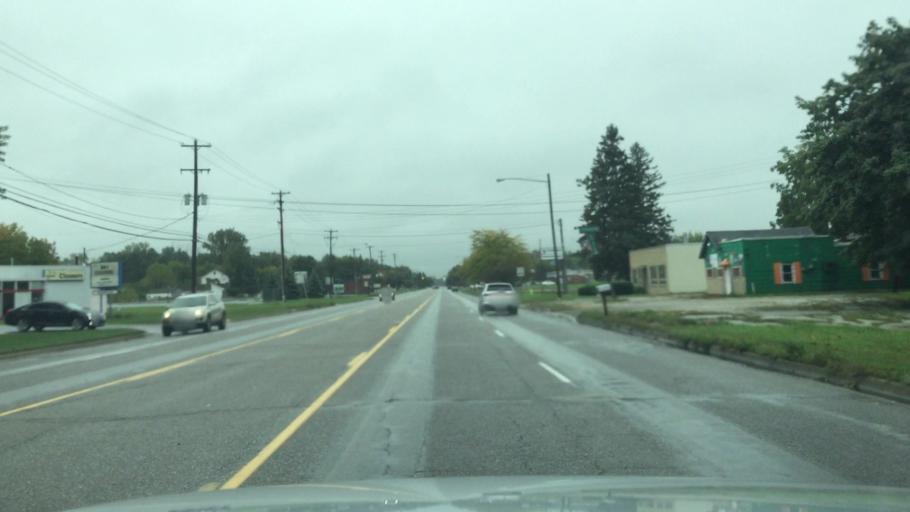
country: US
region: Michigan
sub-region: Saginaw County
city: Bridgeport
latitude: 43.3826
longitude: -83.8991
